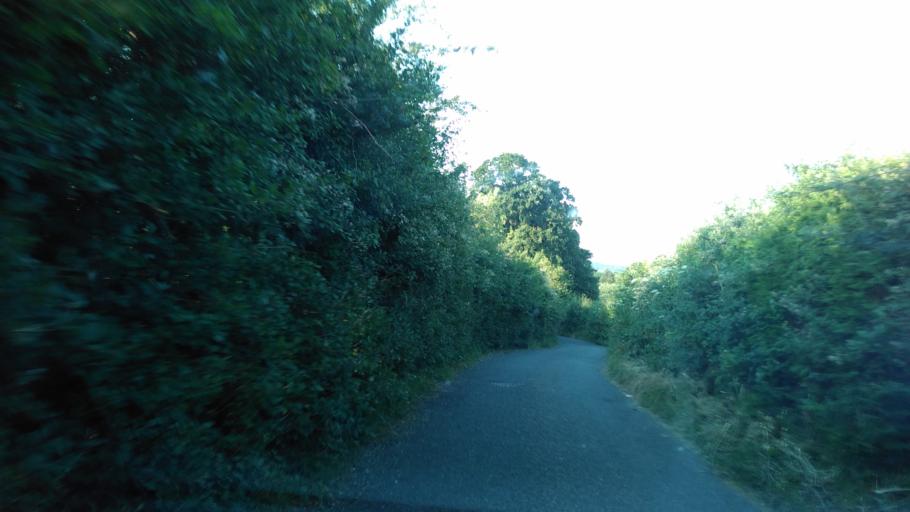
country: GB
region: England
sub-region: Kent
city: Chartham
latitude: 51.2686
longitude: 1.0140
